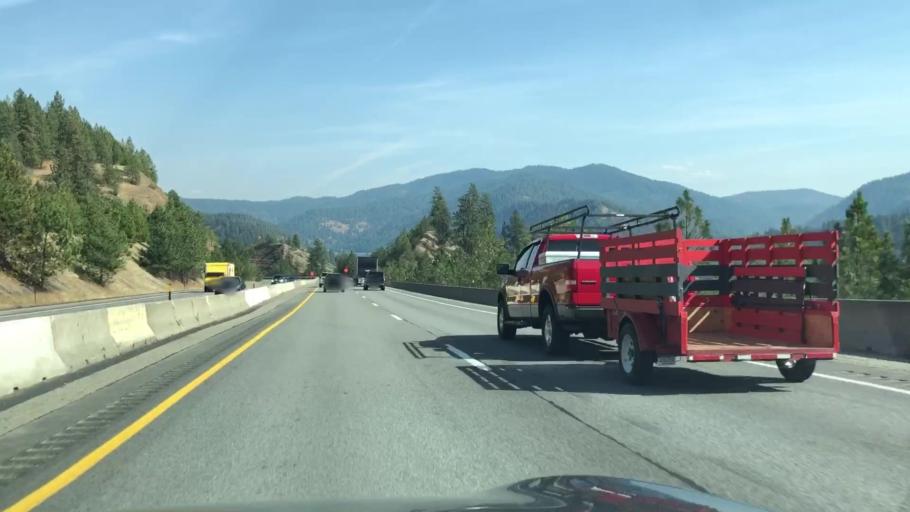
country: US
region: Idaho
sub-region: Kootenai County
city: Coeur d'Alene
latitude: 47.6318
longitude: -116.7042
